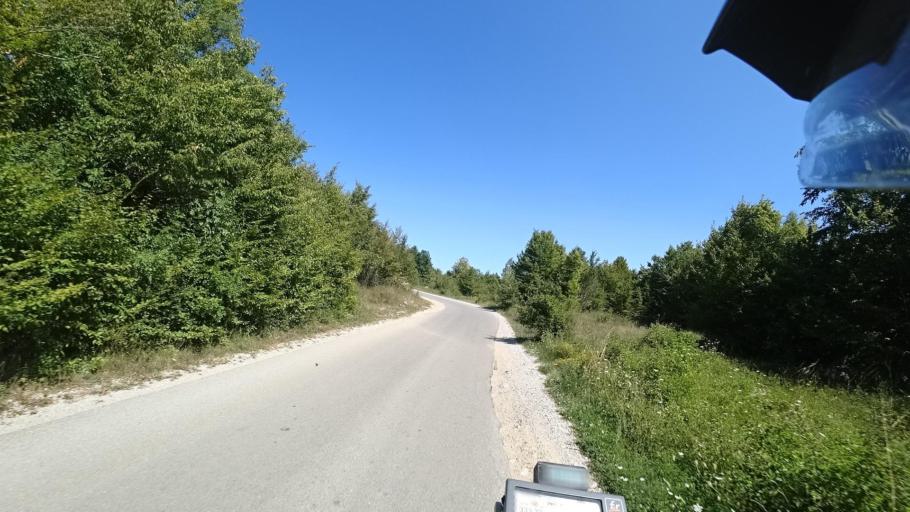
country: HR
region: Licko-Senjska
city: Popovaca
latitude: 44.7296
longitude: 15.2989
